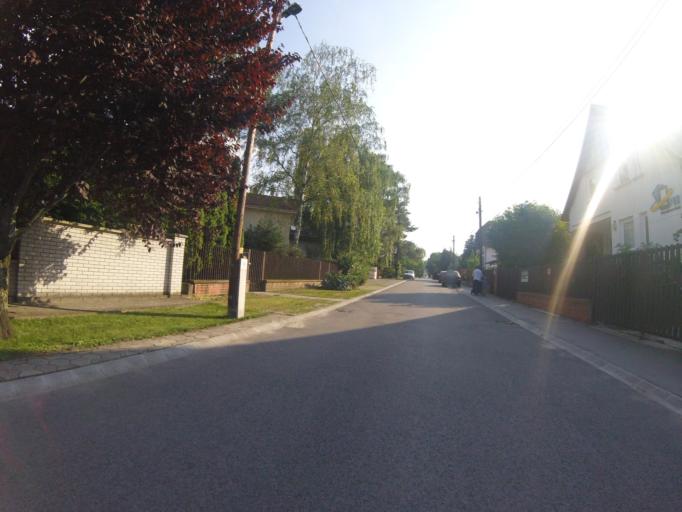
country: HU
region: Pest
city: Budakalasz
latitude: 47.5919
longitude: 19.0577
